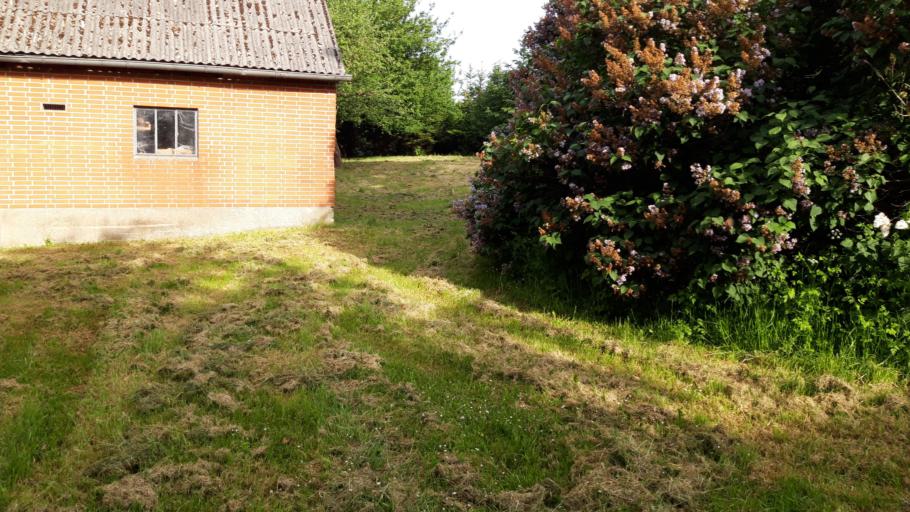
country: DK
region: Central Jutland
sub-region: Arhus Kommune
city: Lystrup
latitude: 56.2293
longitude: 10.1964
